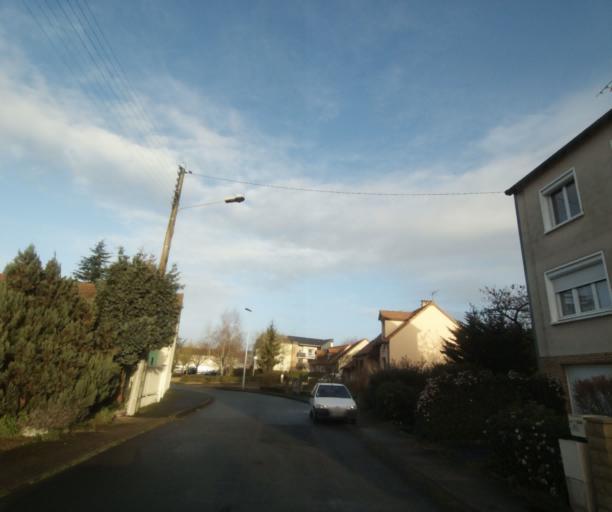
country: FR
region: Pays de la Loire
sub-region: Departement de la Sarthe
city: Le Mans
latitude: 47.9682
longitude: 0.2205
